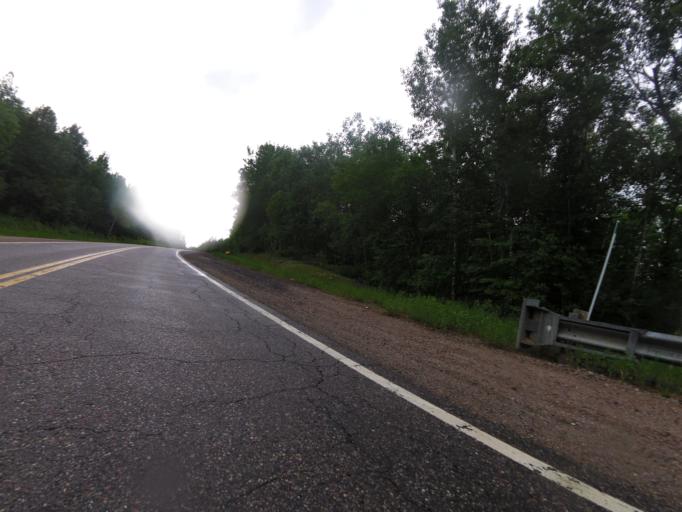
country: CA
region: Quebec
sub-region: Outaouais
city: Shawville
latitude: 45.9059
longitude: -76.2781
